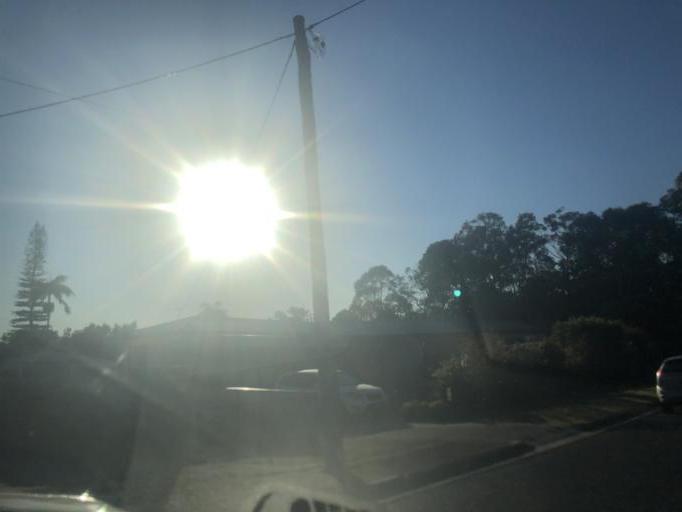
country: AU
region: New South Wales
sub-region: Coffs Harbour
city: Coffs Harbour
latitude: -30.3036
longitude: 153.1222
